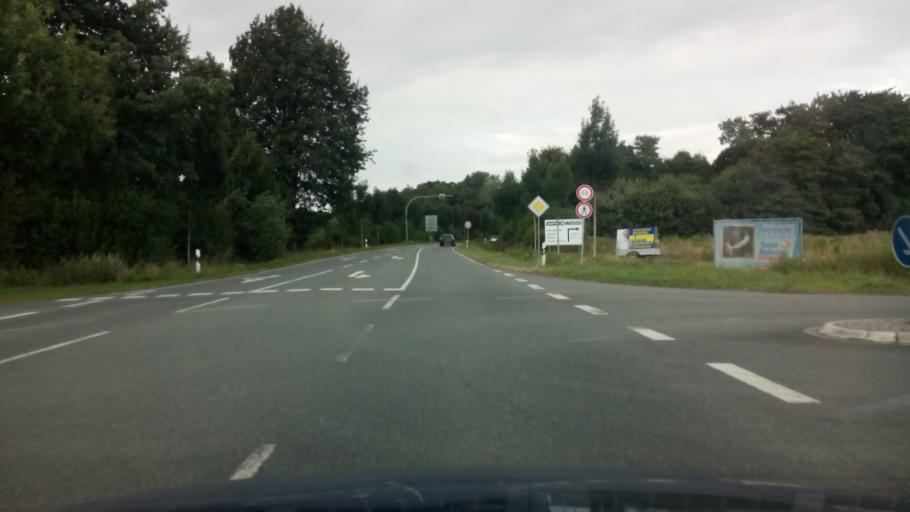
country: DE
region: Lower Saxony
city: Lilienthal
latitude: 53.1568
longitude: 8.9003
